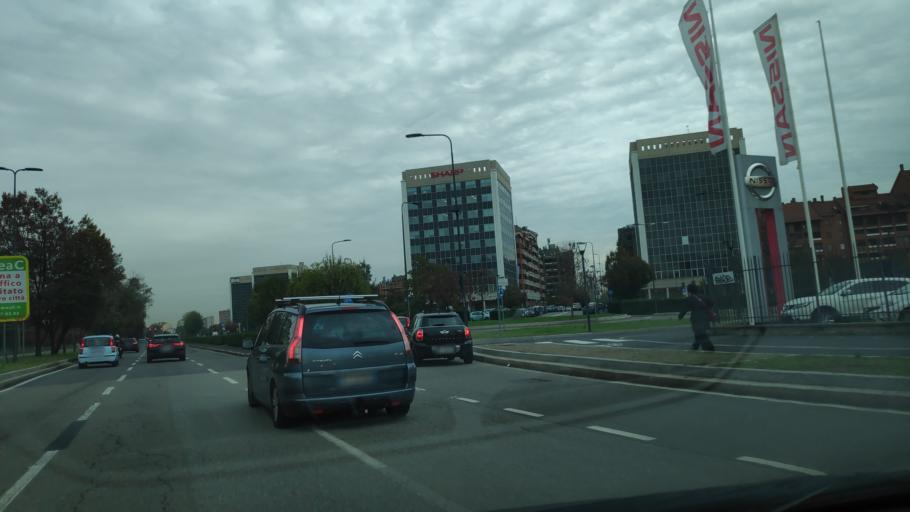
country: IT
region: Lombardy
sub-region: Citta metropolitana di Milano
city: Rozzano
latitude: 45.4149
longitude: 9.1753
